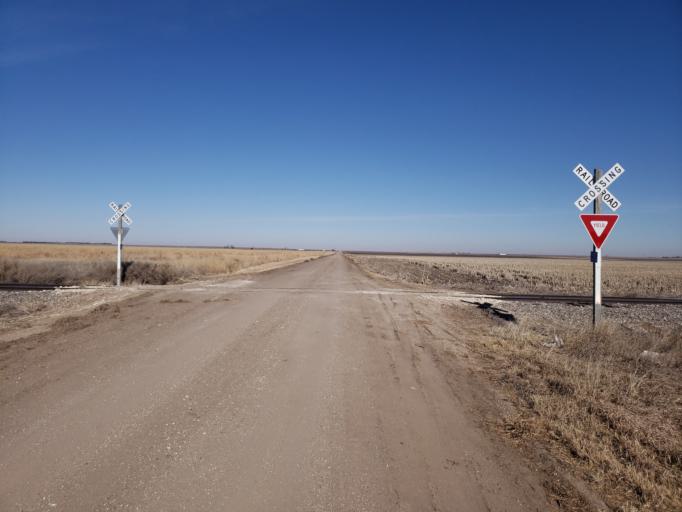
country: US
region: Kansas
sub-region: Ness County
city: Ness City
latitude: 38.4406
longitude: -99.7519
